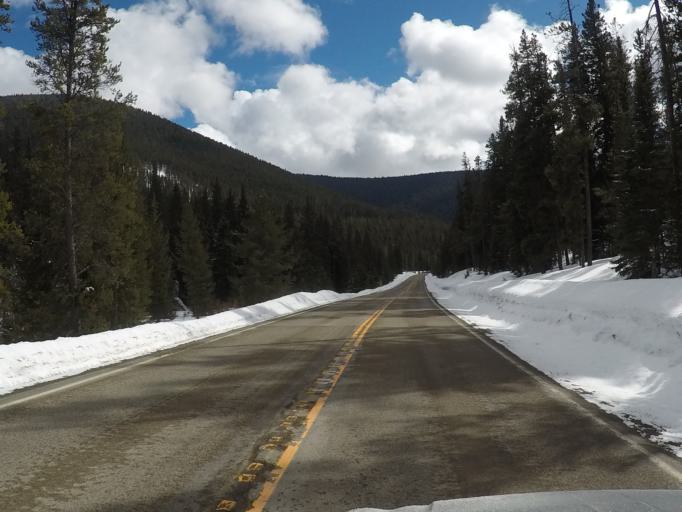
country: US
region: Montana
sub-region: Meagher County
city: White Sulphur Springs
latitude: 46.7879
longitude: -110.6974
